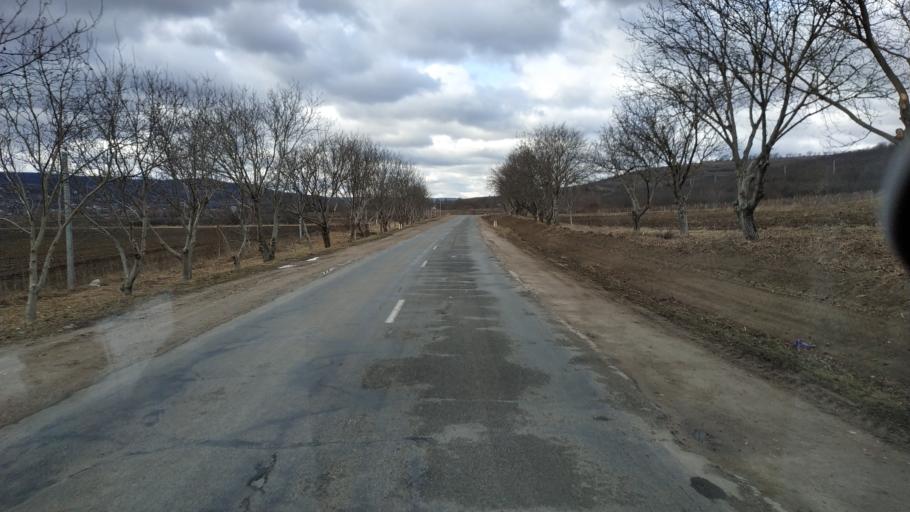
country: MD
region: Stinga Nistrului
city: Bucovat
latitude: 47.1710
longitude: 28.4474
